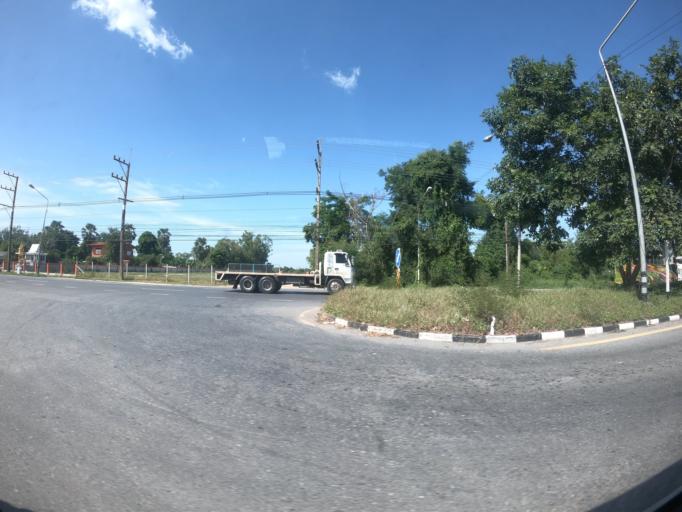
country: TH
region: Nakhon Nayok
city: Ban Na
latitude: 14.2506
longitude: 101.0993
